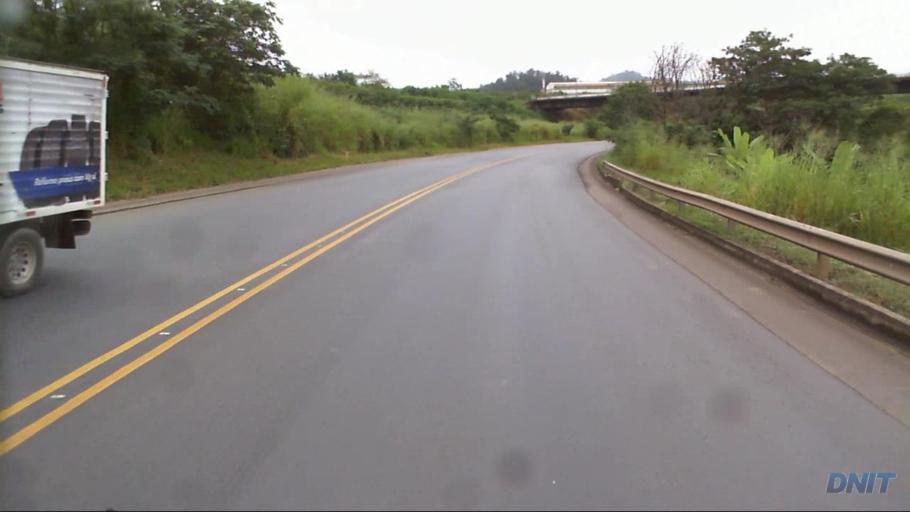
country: BR
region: Minas Gerais
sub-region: Coronel Fabriciano
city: Coronel Fabriciano
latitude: -19.5339
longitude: -42.6250
